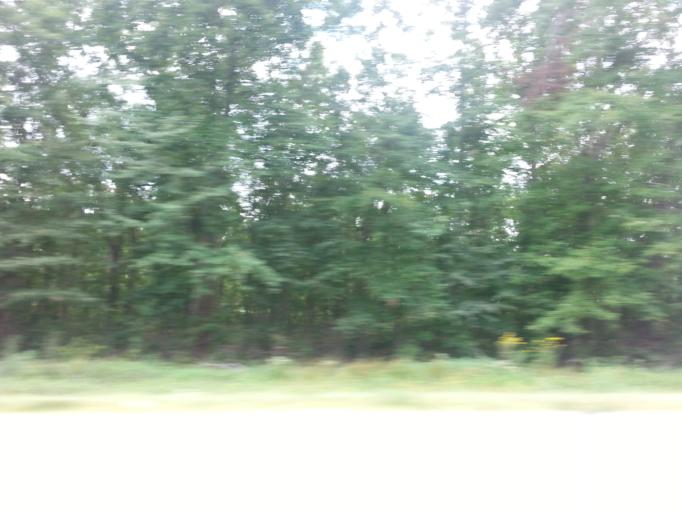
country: US
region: Tennessee
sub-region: Putnam County
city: Monterey
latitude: 36.0798
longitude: -85.2090
